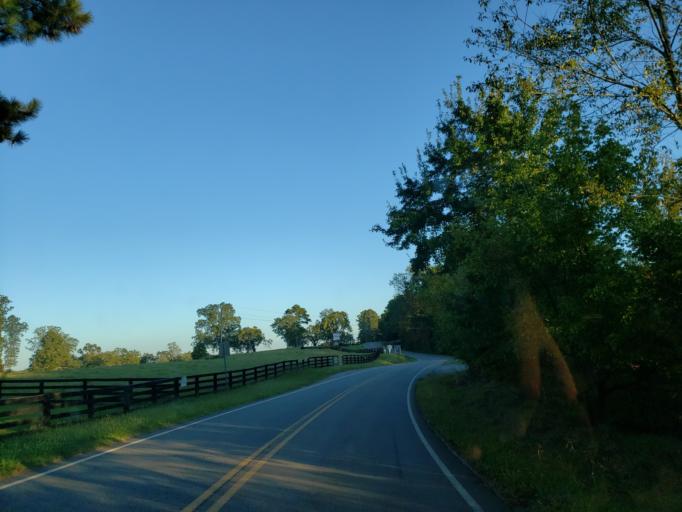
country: US
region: Georgia
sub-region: Bartow County
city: Rydal
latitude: 34.3468
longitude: -84.5809
